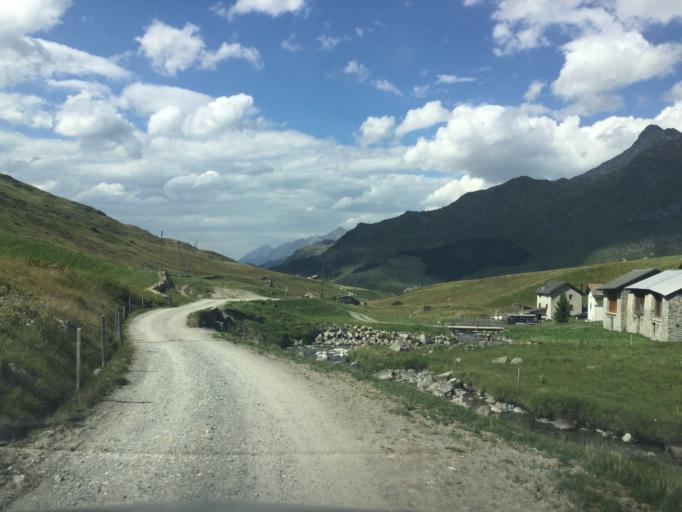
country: CH
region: Grisons
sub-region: Maloja District
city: Silvaplana
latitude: 46.4485
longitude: 9.6573
